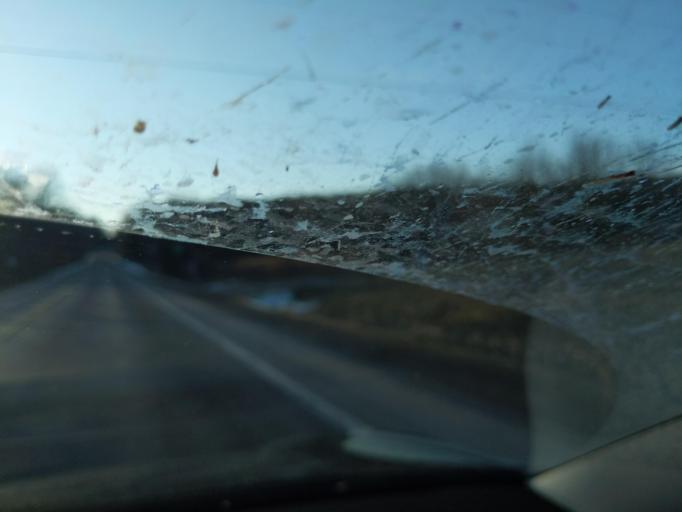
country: US
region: Michigan
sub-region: Ingham County
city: Mason
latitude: 42.5561
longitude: -84.3616
